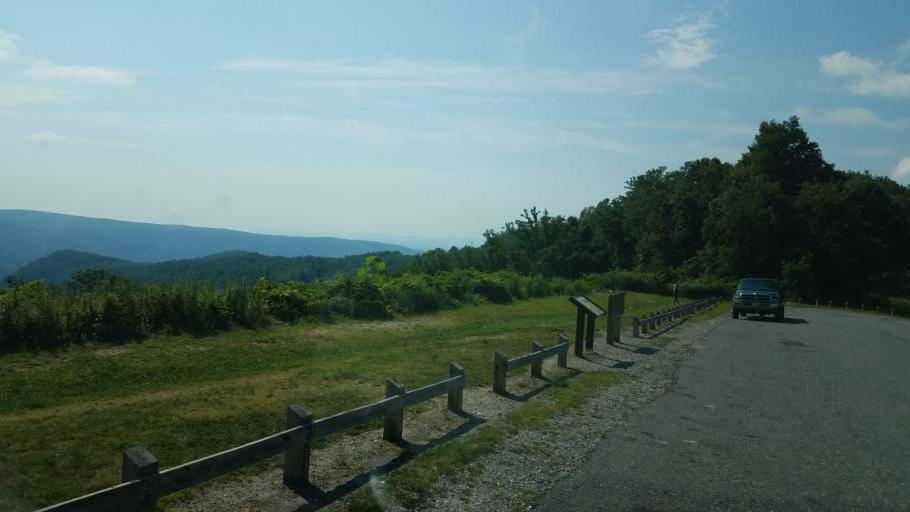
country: US
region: North Carolina
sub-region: Avery County
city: Newland
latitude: 35.9423
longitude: -81.8421
